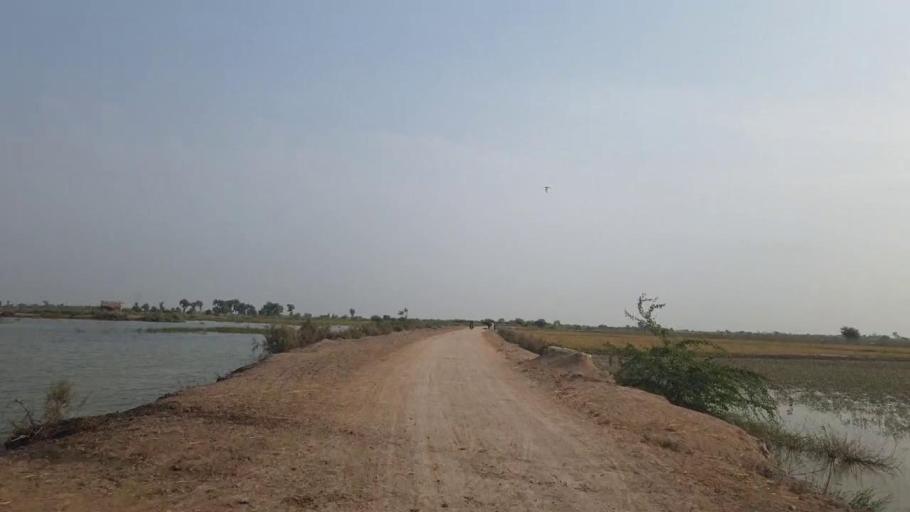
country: PK
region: Sindh
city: Badin
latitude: 24.6053
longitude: 68.6930
